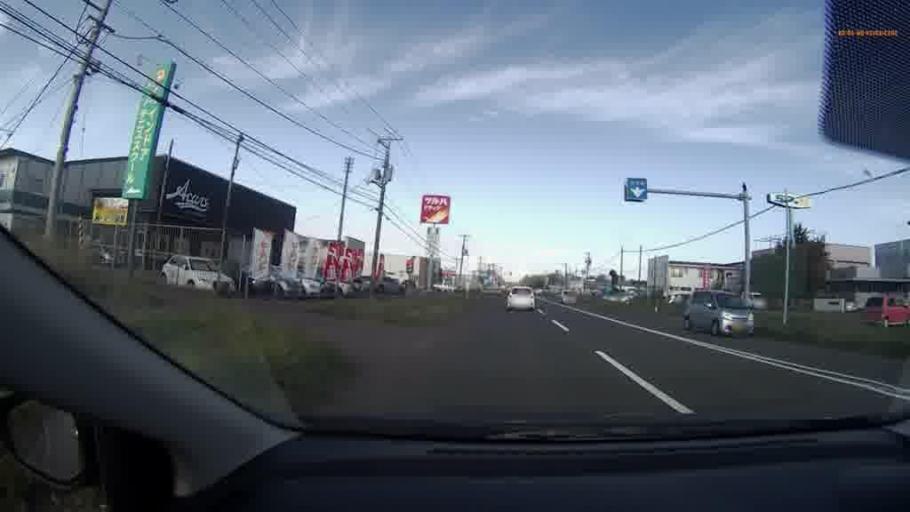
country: JP
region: Hokkaido
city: Kushiro
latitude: 43.0117
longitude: 144.4089
